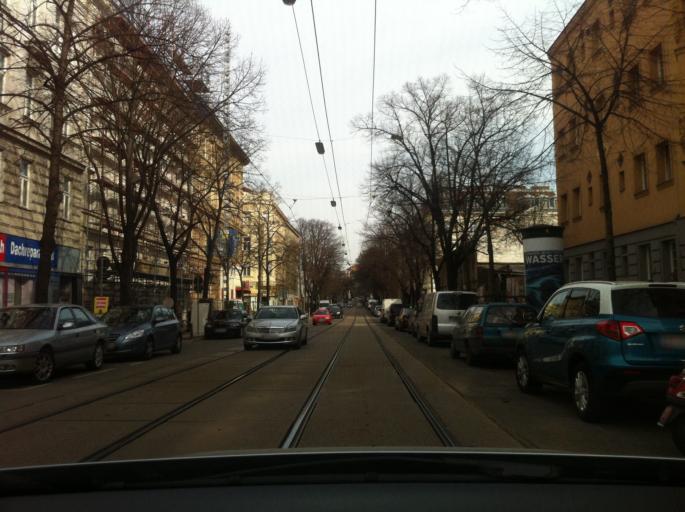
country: AT
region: Lower Austria
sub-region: Politischer Bezirk Modling
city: Perchtoldsdorf
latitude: 48.1974
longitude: 16.2830
